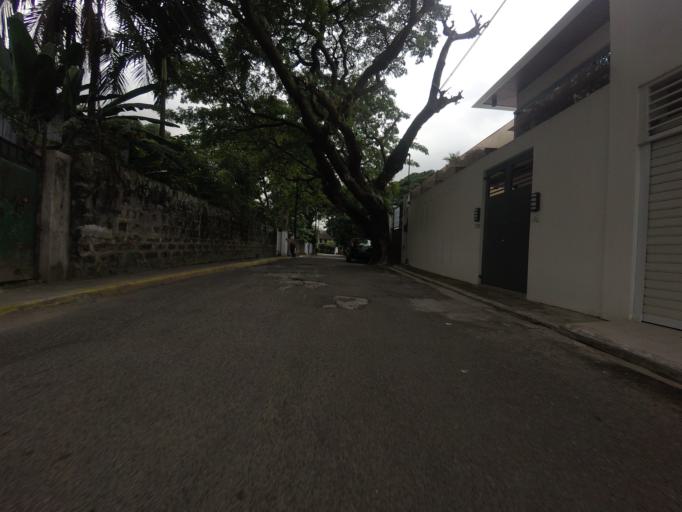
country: PH
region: Metro Manila
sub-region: Mandaluyong
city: Mandaluyong City
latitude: 14.5908
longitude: 121.0443
